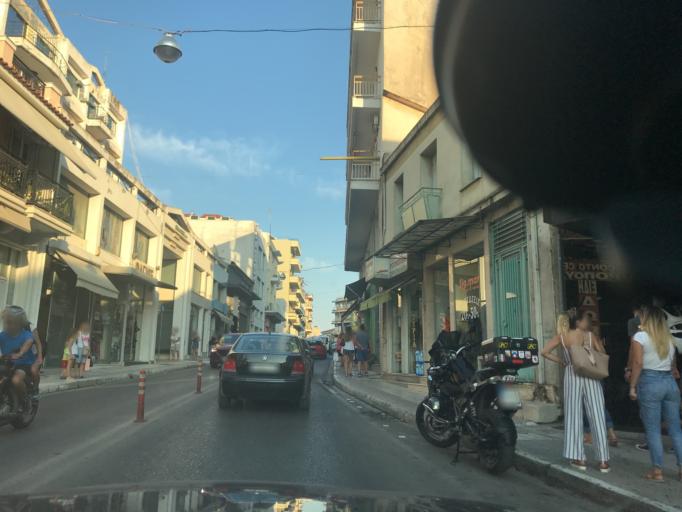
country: GR
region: West Greece
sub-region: Nomos Ileias
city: Pyrgos
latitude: 37.6732
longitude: 21.4379
